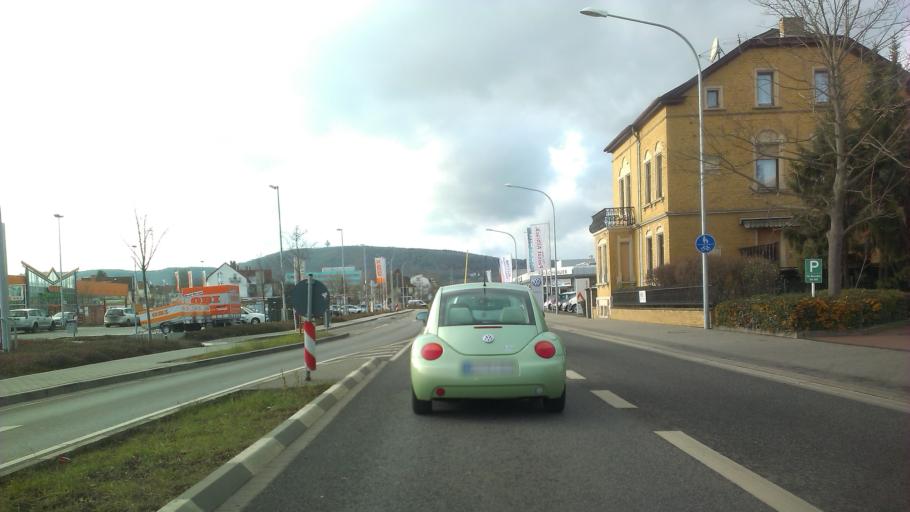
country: DE
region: Rheinland-Pfalz
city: Bad Kreuznach
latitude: 49.8432
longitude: 7.8720
